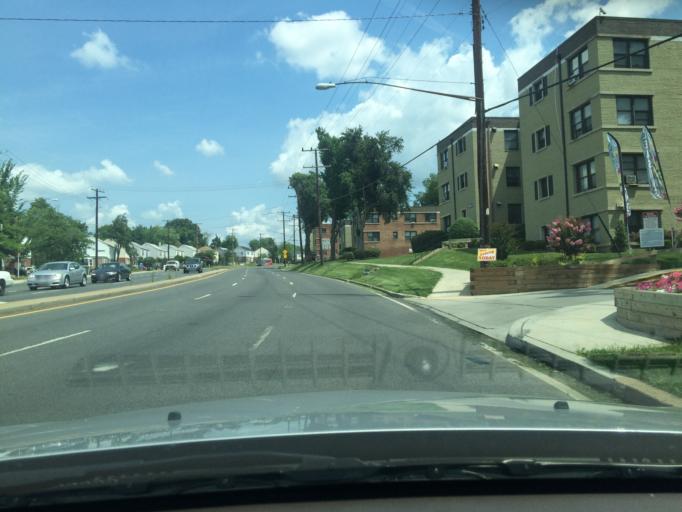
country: US
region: Maryland
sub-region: Prince George's County
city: Chillum
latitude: 38.9726
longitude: -76.9793
